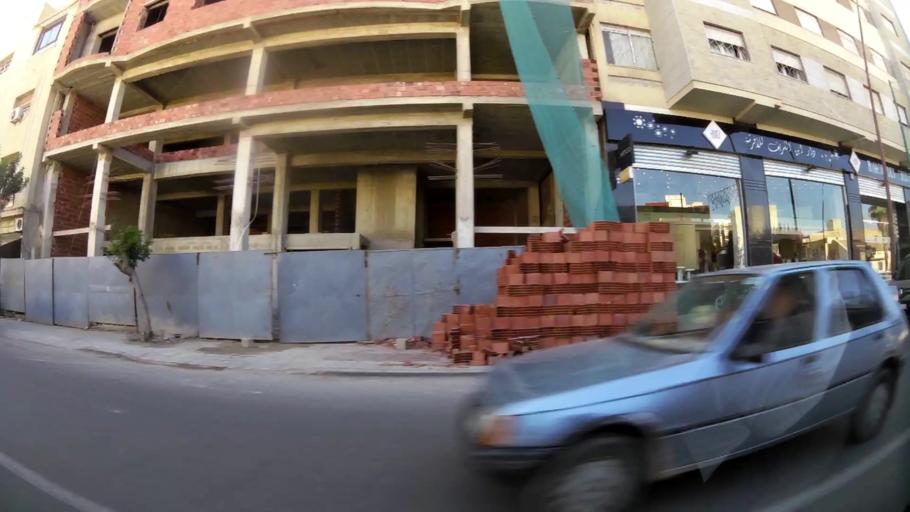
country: MA
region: Oriental
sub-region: Oujda-Angad
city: Oujda
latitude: 34.6872
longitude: -1.9196
